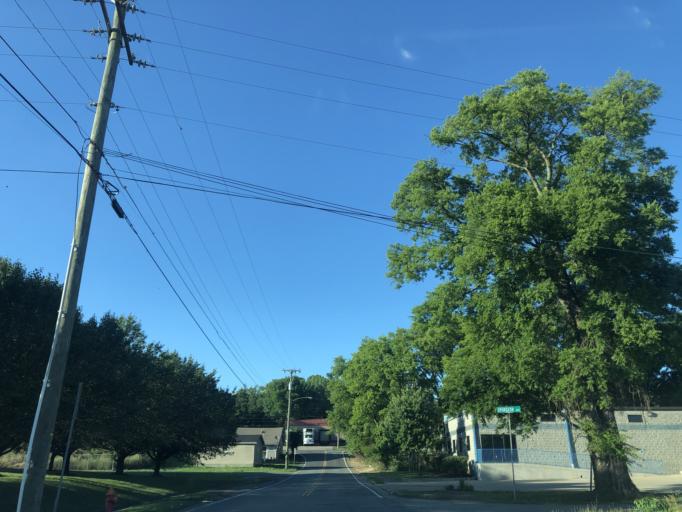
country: US
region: Tennessee
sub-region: Davidson County
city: Nashville
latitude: 36.1939
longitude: -86.7806
